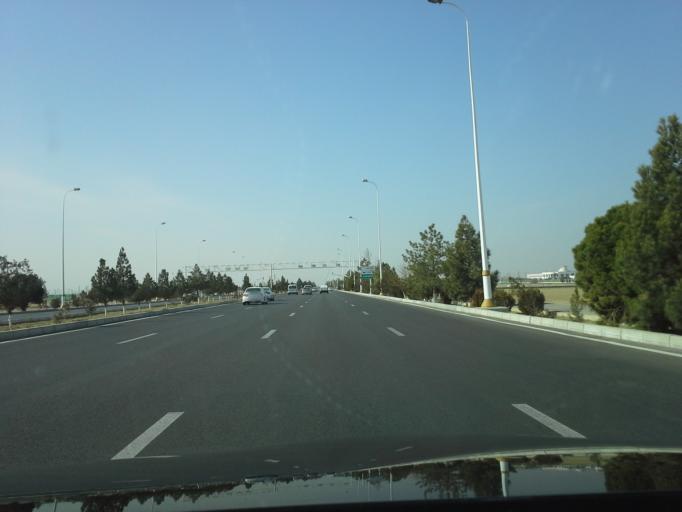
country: TM
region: Ahal
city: Ashgabat
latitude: 37.9994
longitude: 58.3020
